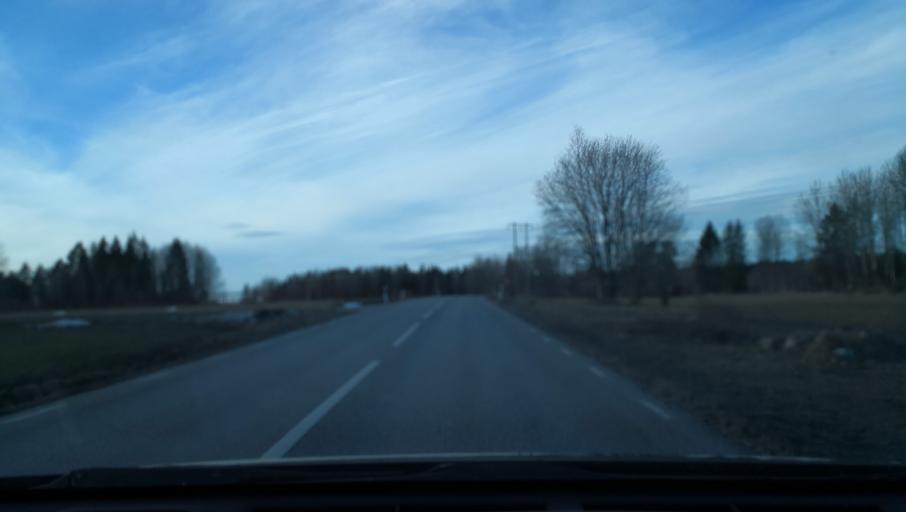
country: SE
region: Uppsala
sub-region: Osthammars Kommun
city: OEsthammar
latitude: 60.3060
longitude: 18.2720
